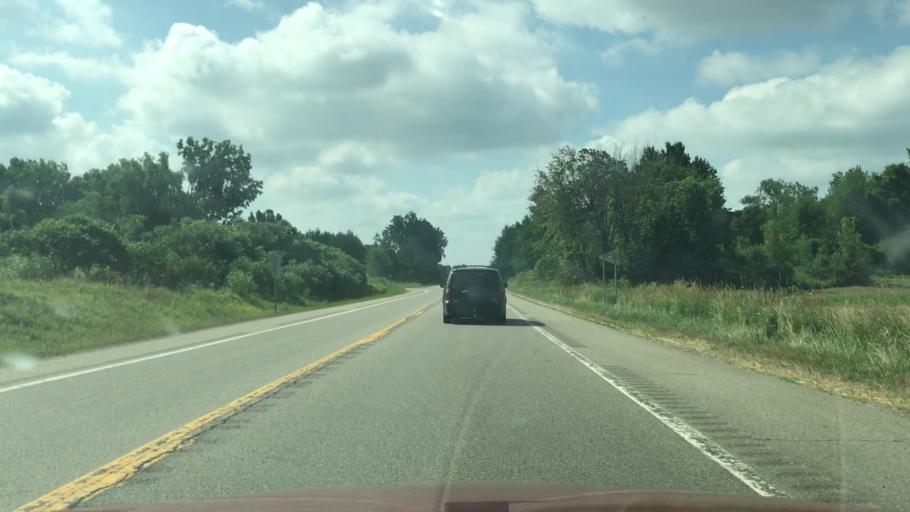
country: US
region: Michigan
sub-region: Kent County
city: Kent City
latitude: 43.2555
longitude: -85.8136
